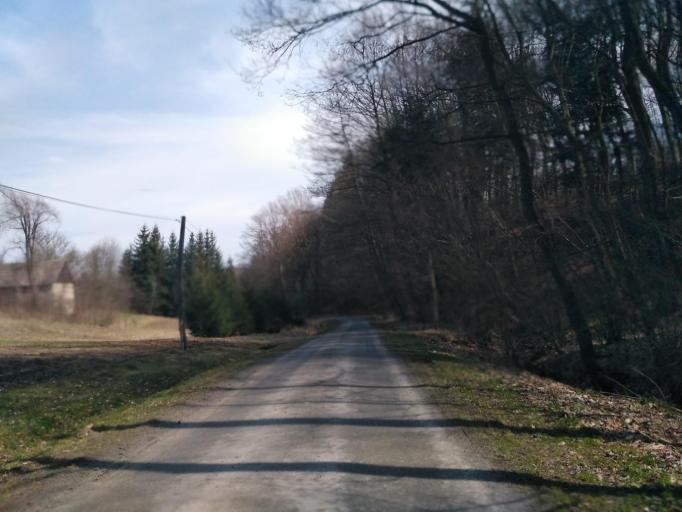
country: PL
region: Subcarpathian Voivodeship
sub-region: Powiat strzyzowski
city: Czudec
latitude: 49.9386
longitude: 21.7796
